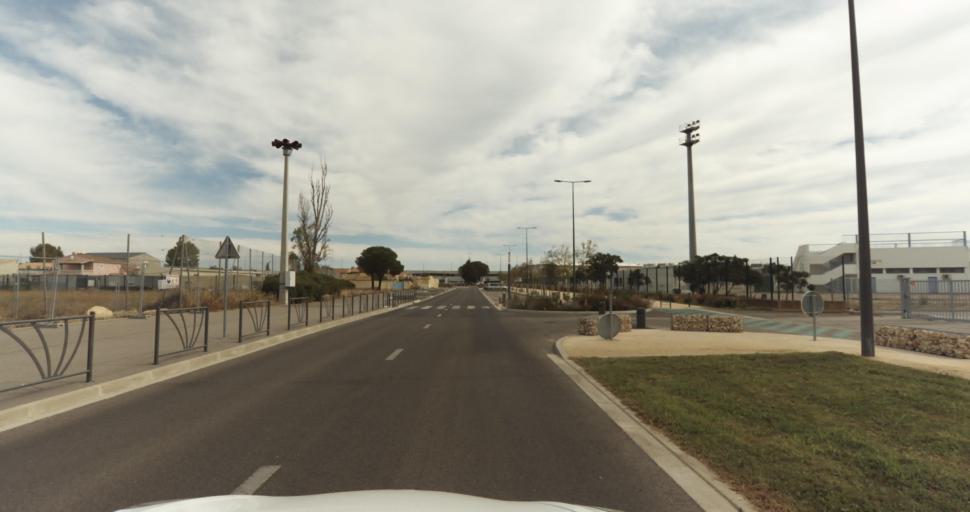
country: FR
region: Provence-Alpes-Cote d'Azur
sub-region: Departement des Bouches-du-Rhone
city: Miramas
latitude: 43.5948
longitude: 4.9987
